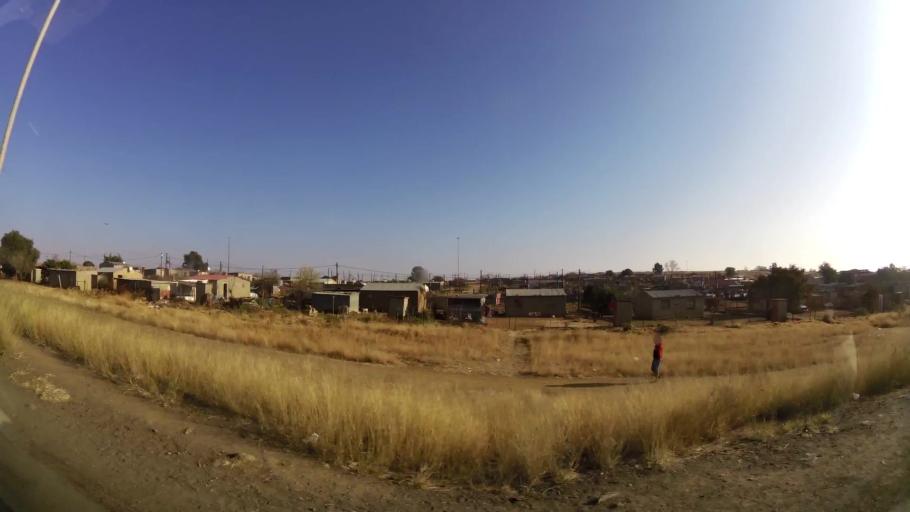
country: ZA
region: Orange Free State
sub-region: Mangaung Metropolitan Municipality
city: Bloemfontein
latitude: -29.1677
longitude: 26.2472
